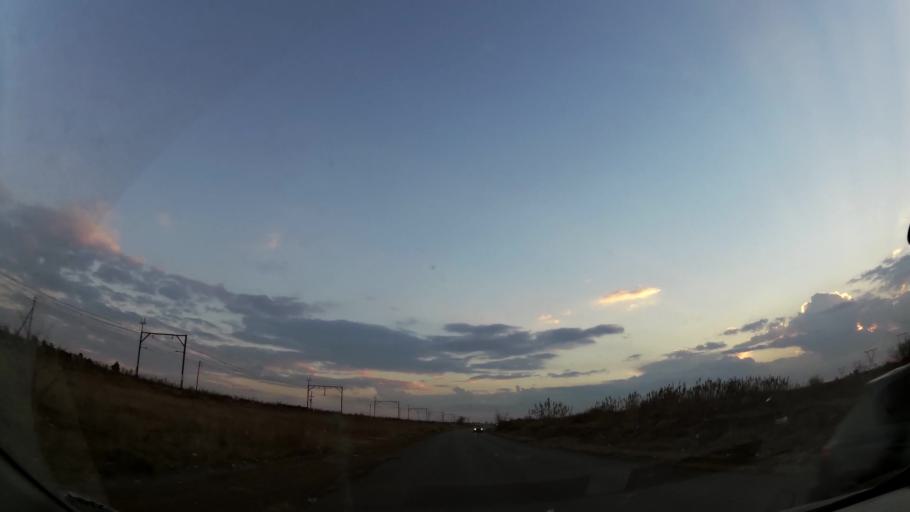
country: ZA
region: Gauteng
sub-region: City of Johannesburg Metropolitan Municipality
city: Orange Farm
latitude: -26.5616
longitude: 27.8726
